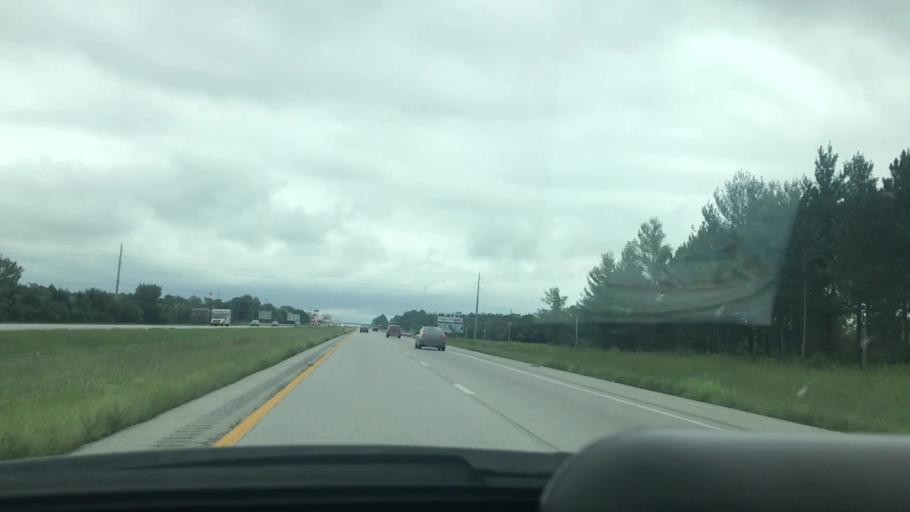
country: US
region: Missouri
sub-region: Jasper County
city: Duquesne
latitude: 37.0485
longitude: -94.4650
